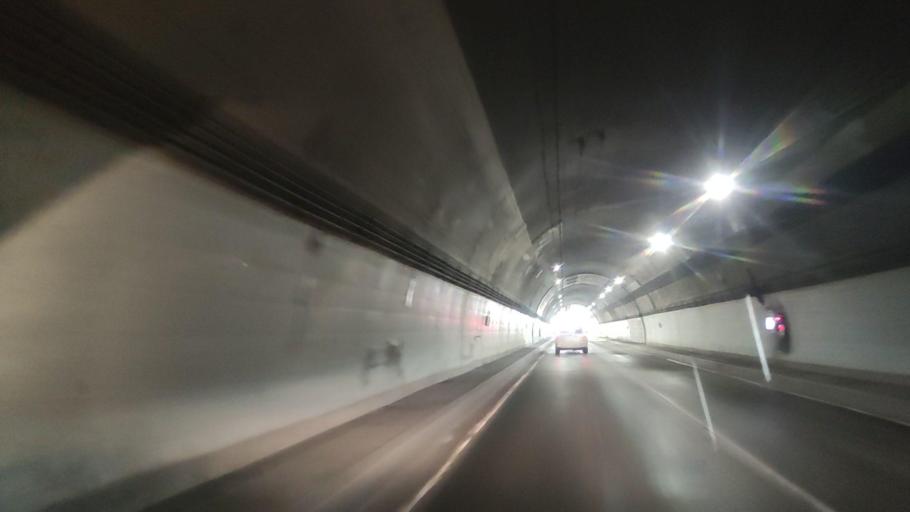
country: JP
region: Hokkaido
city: Ishikari
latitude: 43.4403
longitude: 141.4151
